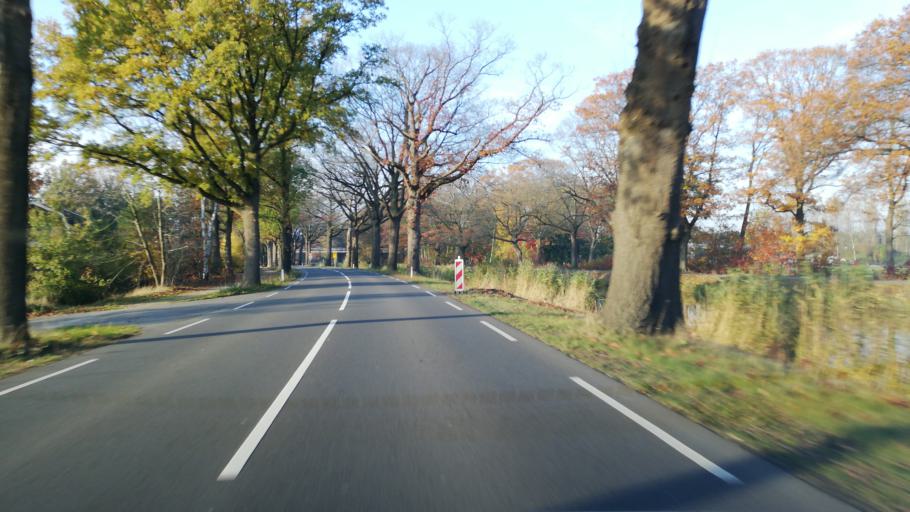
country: NL
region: Gelderland
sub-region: Gemeente Apeldoorn
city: Beekbergen
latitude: 52.1776
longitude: 5.9940
